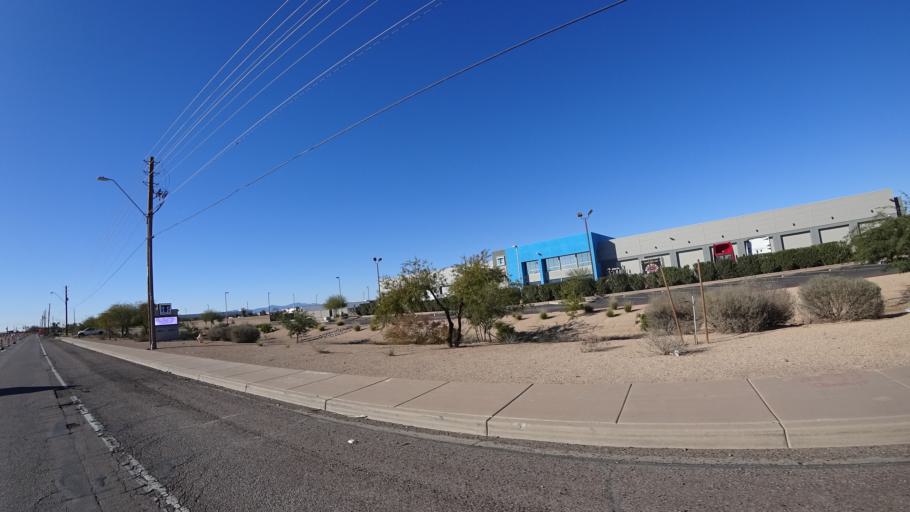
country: US
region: Arizona
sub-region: Maricopa County
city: Tolleson
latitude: 33.4363
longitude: -112.2495
